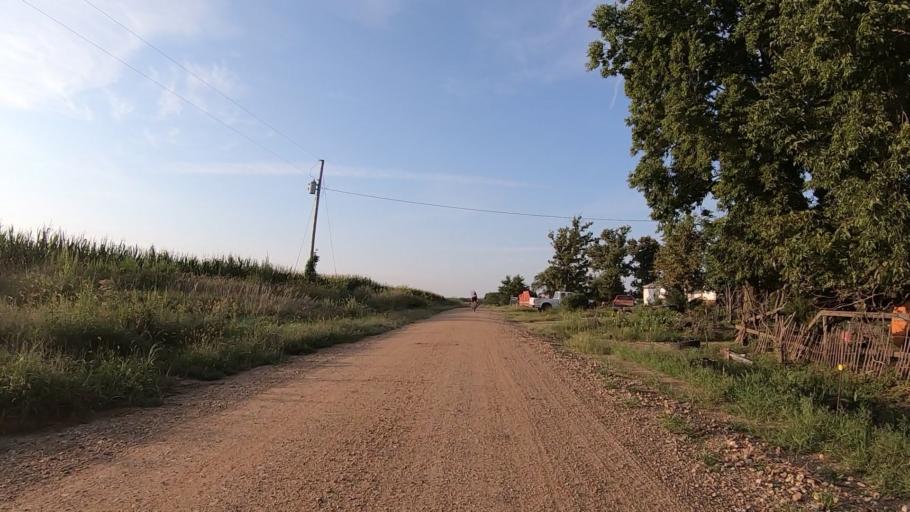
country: US
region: Kansas
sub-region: Marshall County
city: Blue Rapids
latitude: 39.7683
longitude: -96.7508
